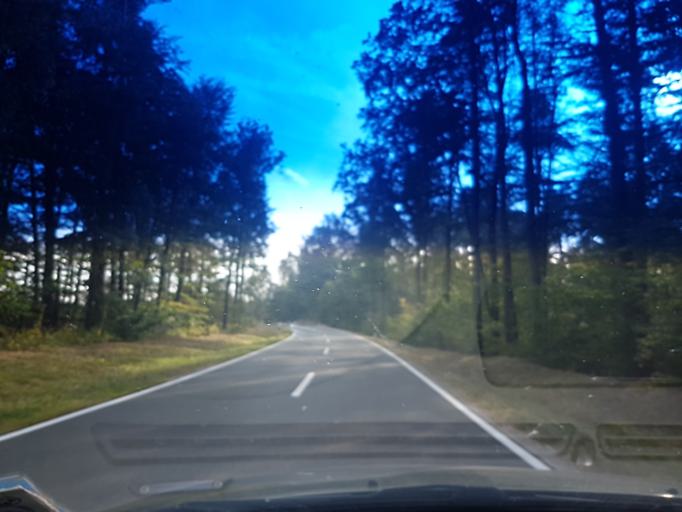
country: DE
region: Bavaria
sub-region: Upper Franconia
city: Burgwindheim
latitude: 49.7876
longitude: 10.5658
